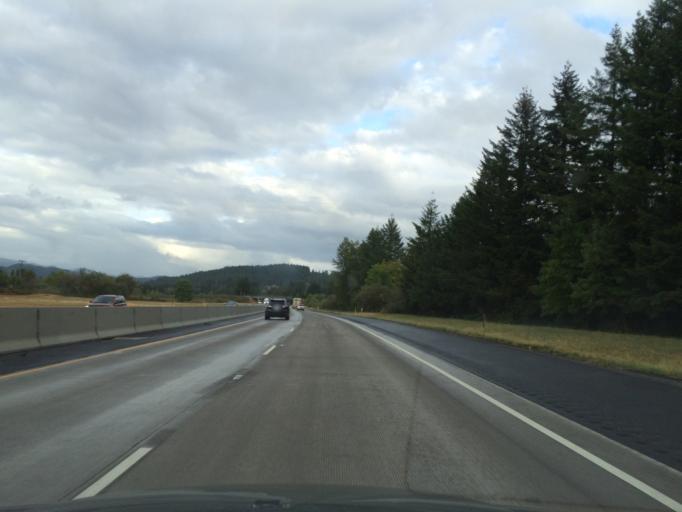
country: US
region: Oregon
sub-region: Lane County
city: Cottage Grove
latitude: 43.7498
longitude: -123.1215
